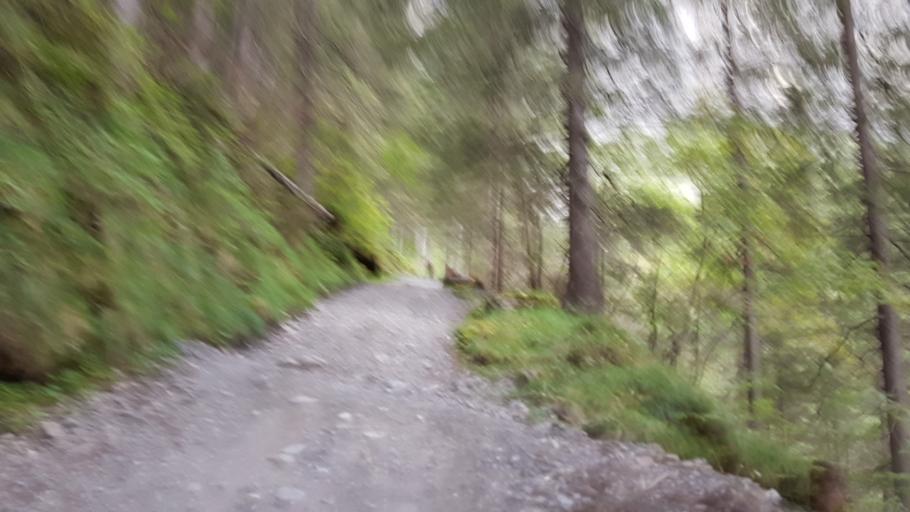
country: CH
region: Bern
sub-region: Frutigen-Niedersimmental District
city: Kandersteg
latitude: 46.4720
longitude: 7.6546
